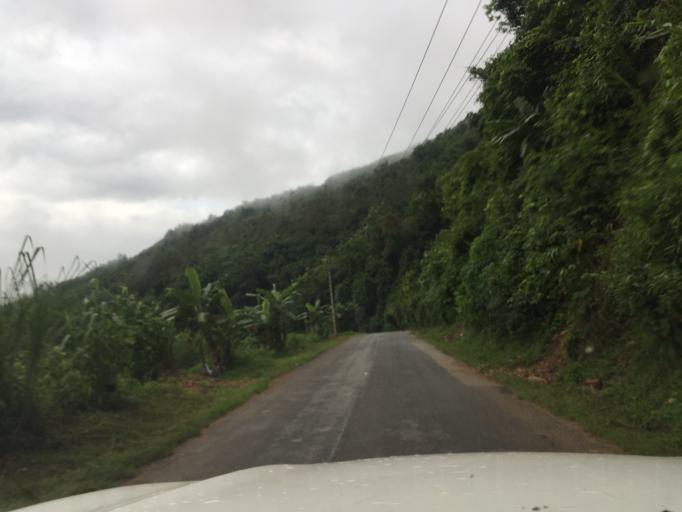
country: LA
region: Oudomxai
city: Muang La
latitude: 20.9065
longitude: 102.1807
